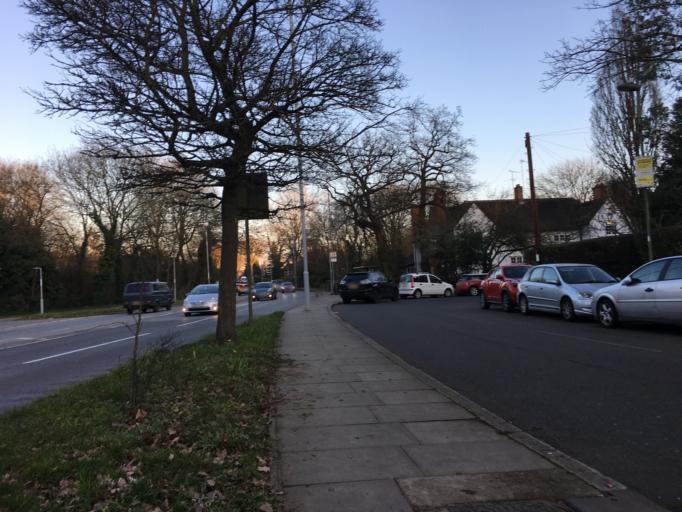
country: GB
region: England
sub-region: Greater London
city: Hendon
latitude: 51.5869
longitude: -0.1913
